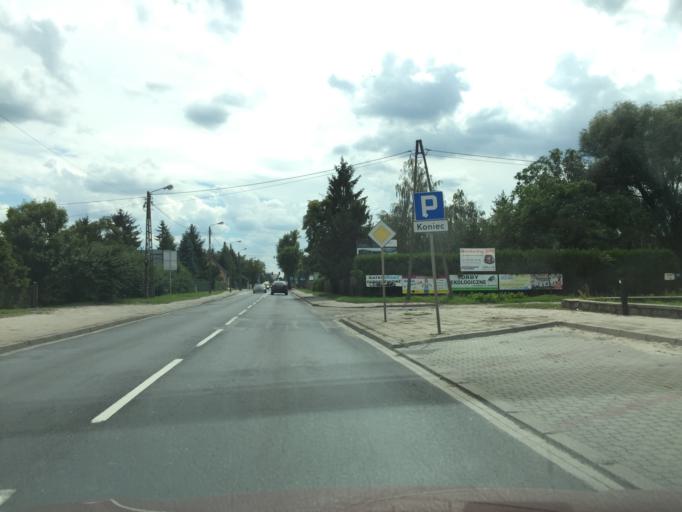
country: PL
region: Greater Poland Voivodeship
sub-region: Kalisz
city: Kalisz
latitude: 51.7417
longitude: 18.0965
